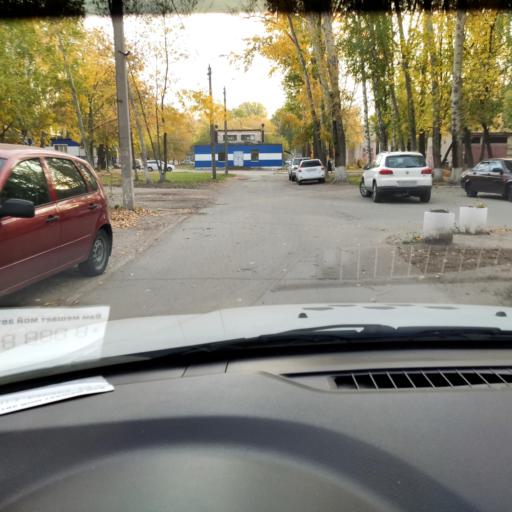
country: RU
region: Samara
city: Tol'yatti
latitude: 53.5010
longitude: 49.4106
